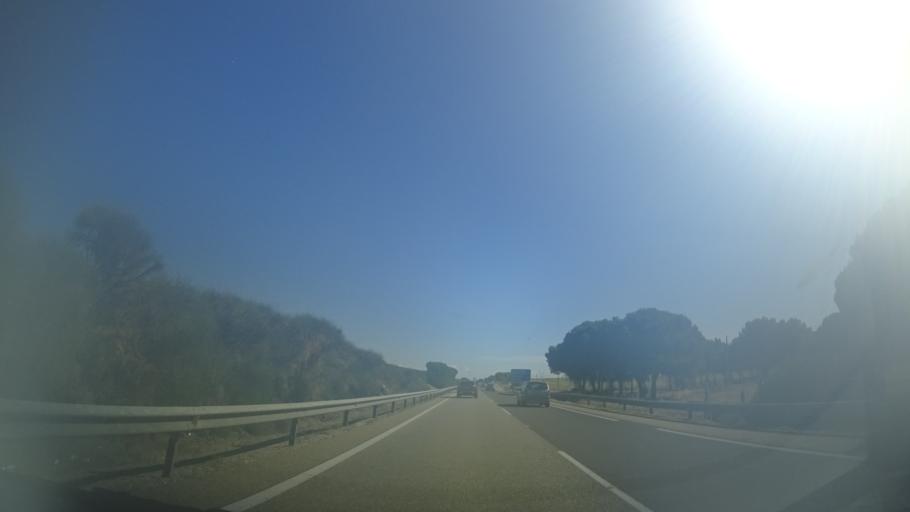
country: ES
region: Castille and Leon
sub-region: Provincia de Valladolid
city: Rueda
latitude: 41.4558
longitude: -4.9822
